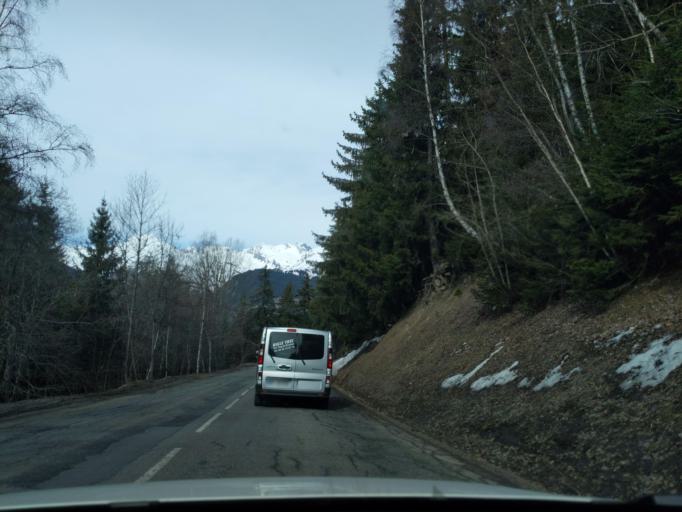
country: FR
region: Rhone-Alpes
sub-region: Departement de la Savoie
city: Bourg-Saint-Maurice
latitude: 45.5915
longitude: 6.7787
